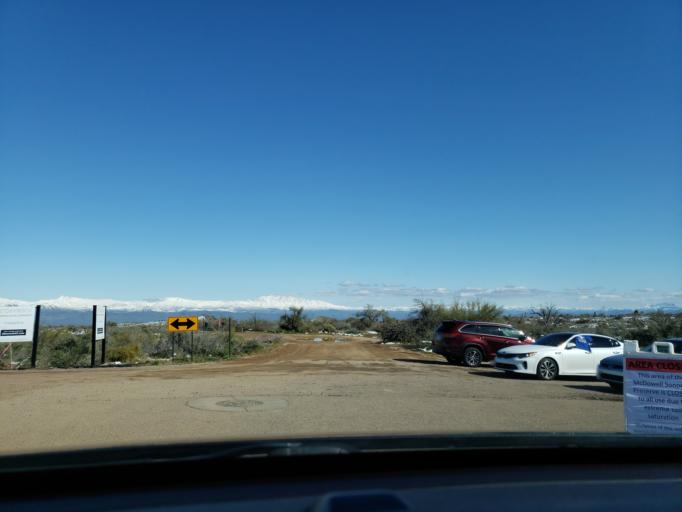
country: US
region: Arizona
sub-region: Maricopa County
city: Rio Verde
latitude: 33.7126
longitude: -111.8049
